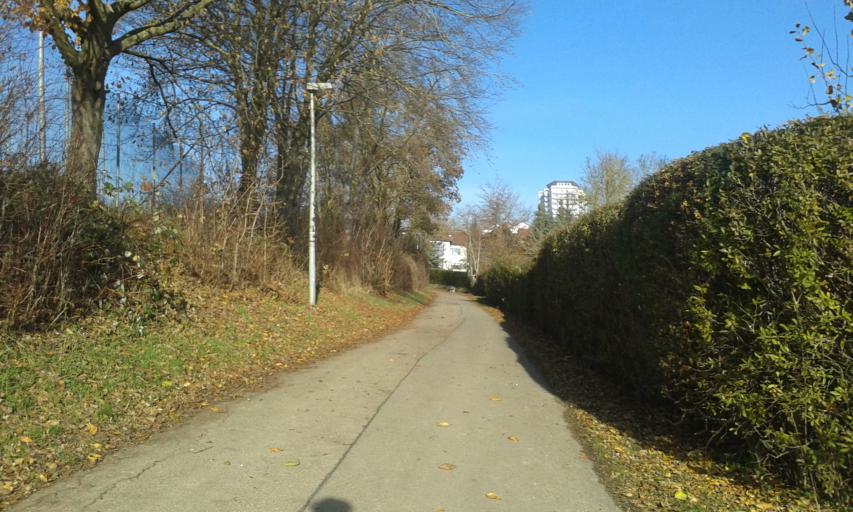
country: DE
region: Baden-Wuerttemberg
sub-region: Tuebingen Region
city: Ulm
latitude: 48.4056
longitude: 9.9594
